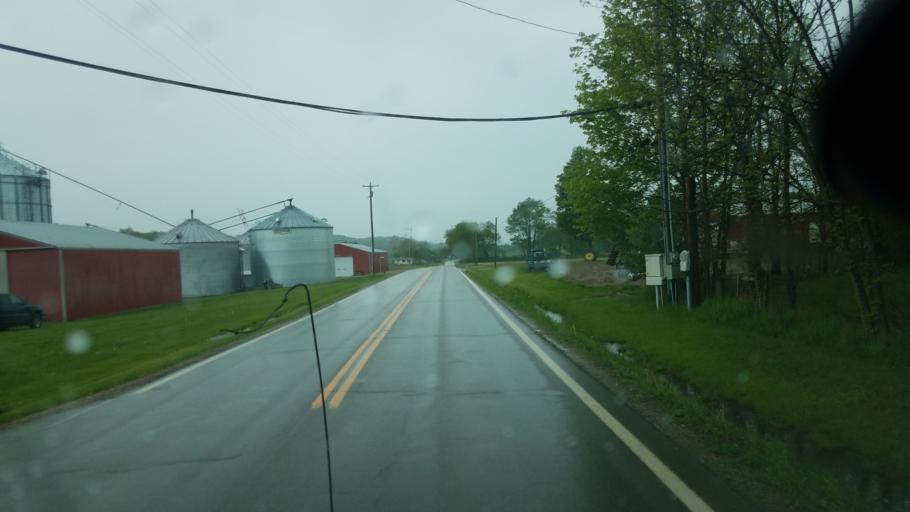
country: US
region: Ohio
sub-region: Muskingum County
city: Dresden
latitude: 40.1889
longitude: -82.0378
